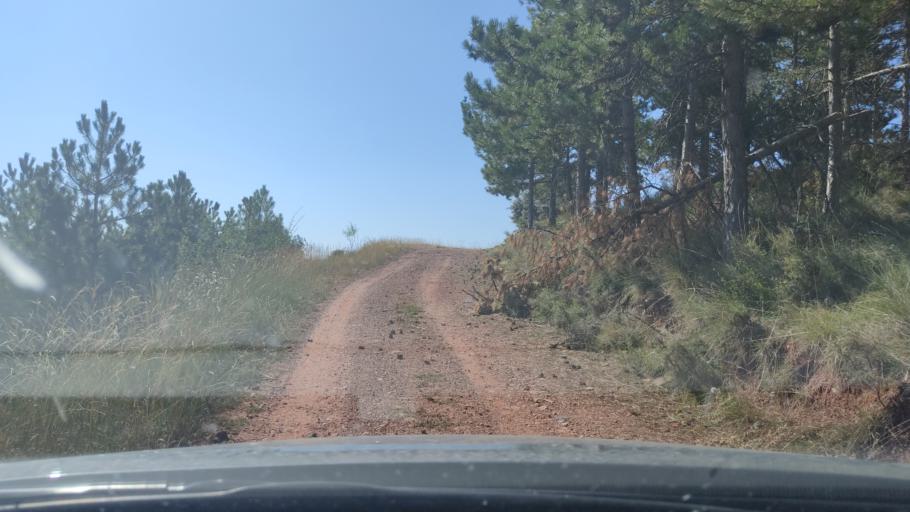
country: ES
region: Aragon
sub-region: Provincia de Teruel
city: Monforte de Moyuela
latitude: 41.0424
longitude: -1.0353
